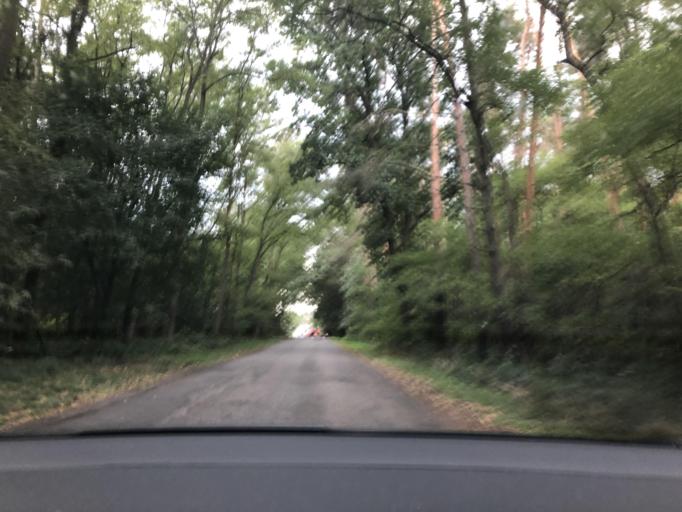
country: CZ
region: Central Bohemia
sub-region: Okres Kolin
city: Tynec nad Labem
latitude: 50.0506
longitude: 15.3731
